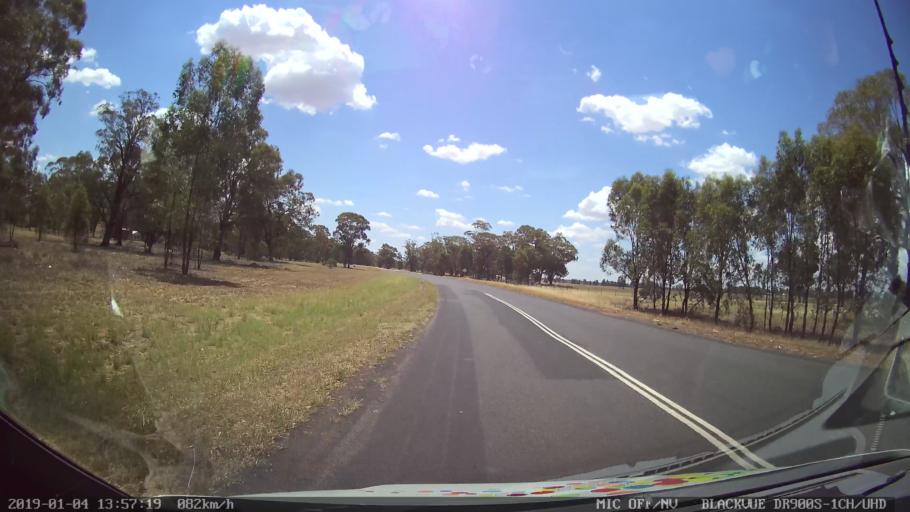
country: AU
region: New South Wales
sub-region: Dubbo Municipality
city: Dubbo
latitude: -32.3415
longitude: 148.6002
